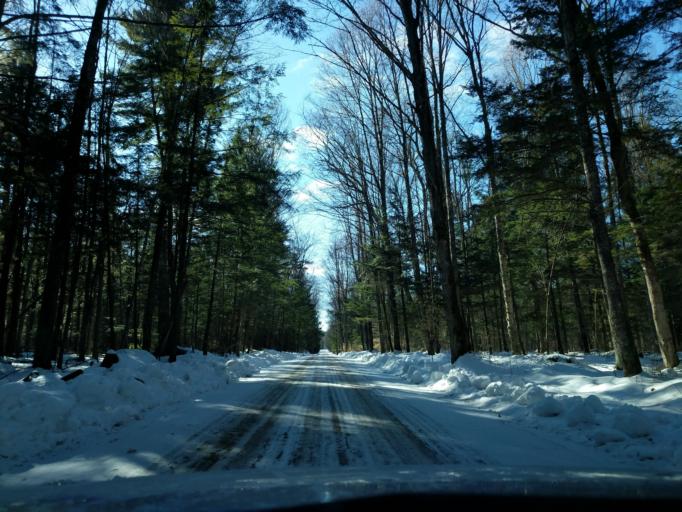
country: US
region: Wisconsin
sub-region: Menominee County
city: Keshena
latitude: 45.0907
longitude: -88.6222
